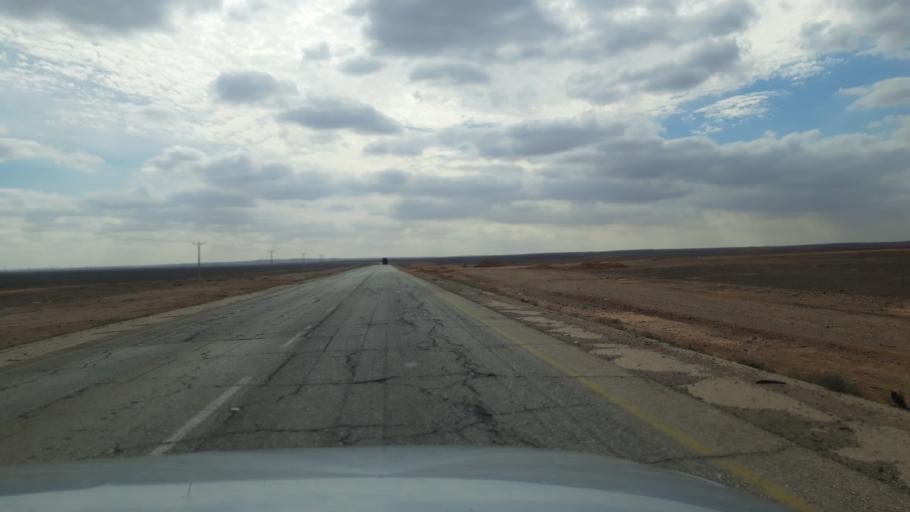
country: JO
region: Amman
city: Al Azraq ash Shamali
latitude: 31.8280
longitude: 36.6187
